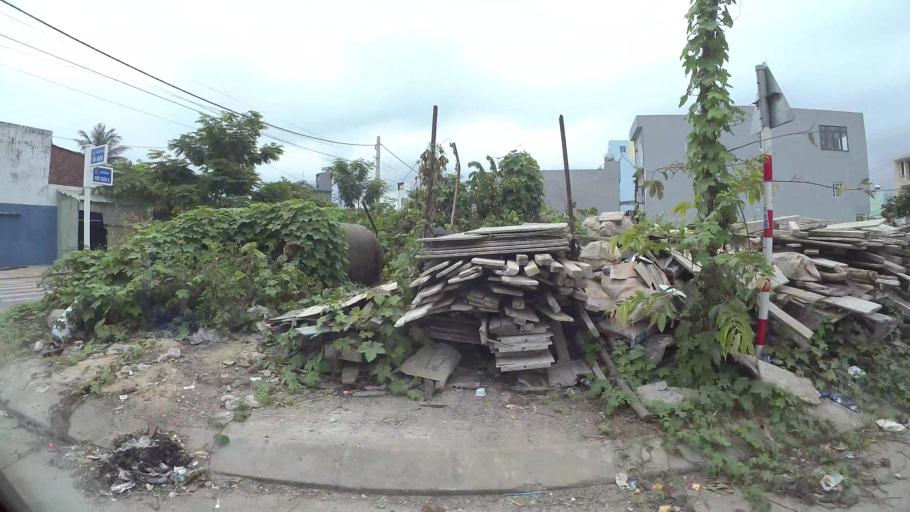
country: VN
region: Da Nang
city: Lien Chieu
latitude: 16.0721
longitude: 108.1662
